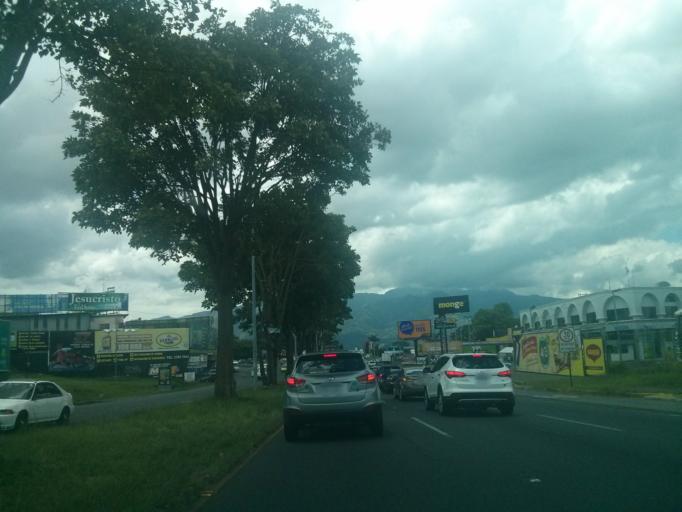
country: CR
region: San Jose
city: San Pedro
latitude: 9.9228
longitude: -84.0581
